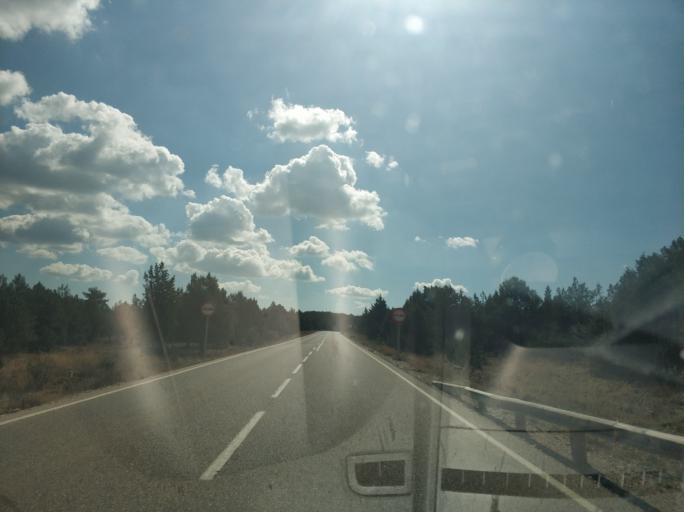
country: ES
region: Castille and Leon
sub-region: Provincia de Soria
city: Ucero
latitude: 41.7348
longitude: -3.0429
